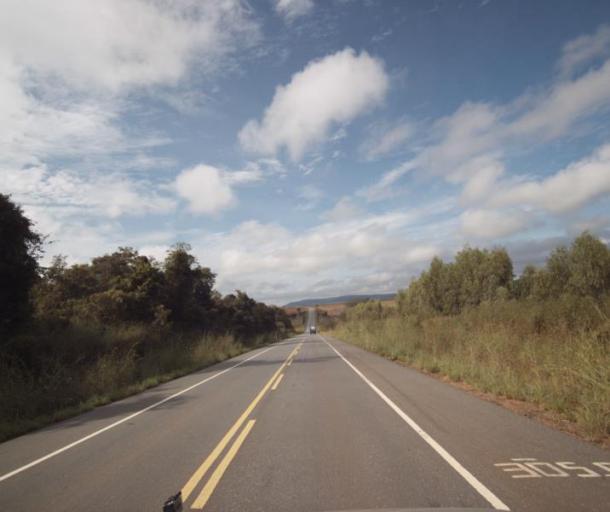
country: BR
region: Goias
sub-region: Barro Alto
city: Barro Alto
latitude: -15.2585
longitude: -48.6873
